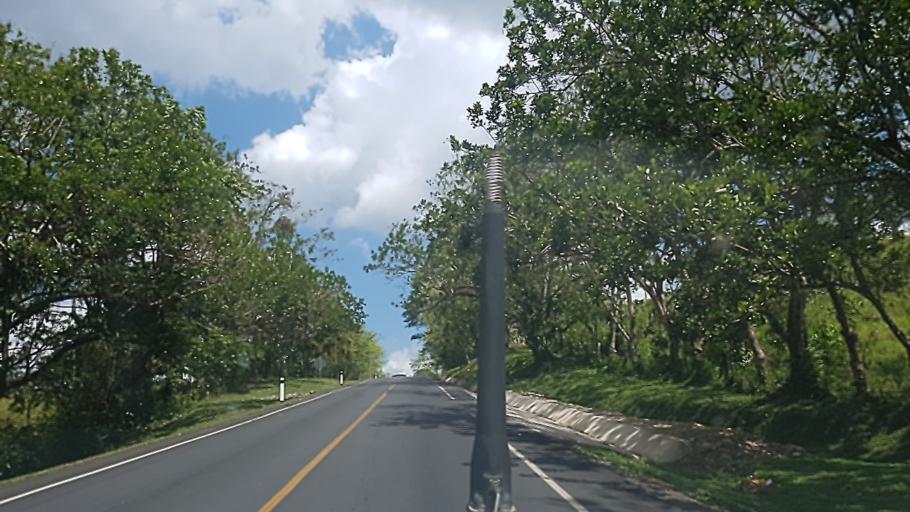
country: NI
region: Atlantico Sur
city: Muelle de los Bueyes
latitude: 11.9881
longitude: -84.7589
